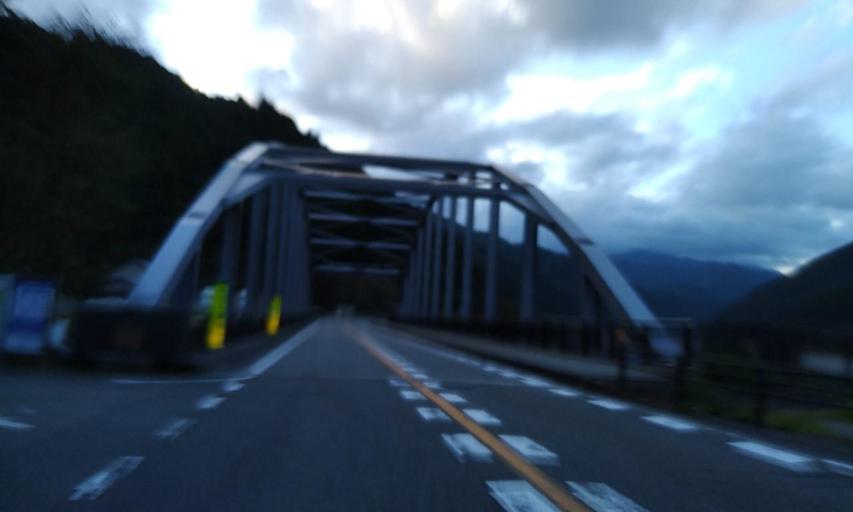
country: JP
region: Wakayama
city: Shingu
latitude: 33.7236
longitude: 135.9646
